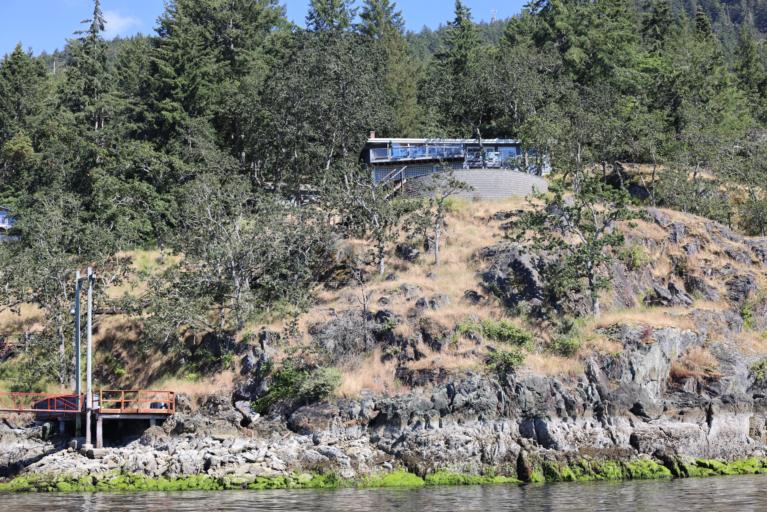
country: CA
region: British Columbia
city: North Cowichan
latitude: 48.8213
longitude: -123.5988
